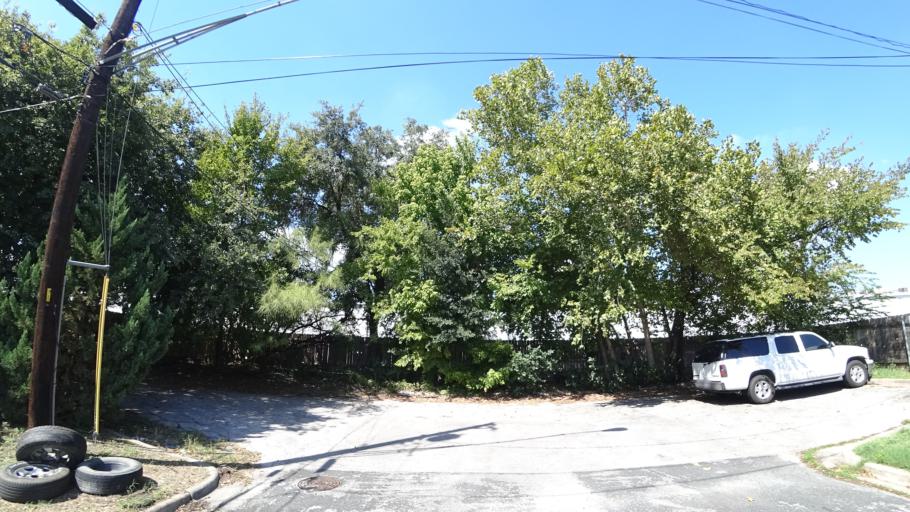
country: US
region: Texas
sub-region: Travis County
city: Austin
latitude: 30.3359
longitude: -97.7165
